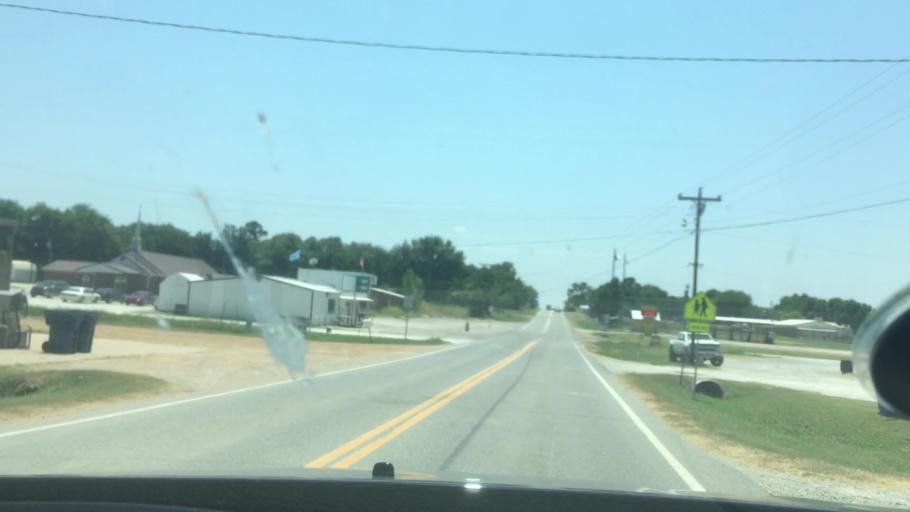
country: US
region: Oklahoma
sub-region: Coal County
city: Coalgate
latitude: 34.6057
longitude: -96.4244
